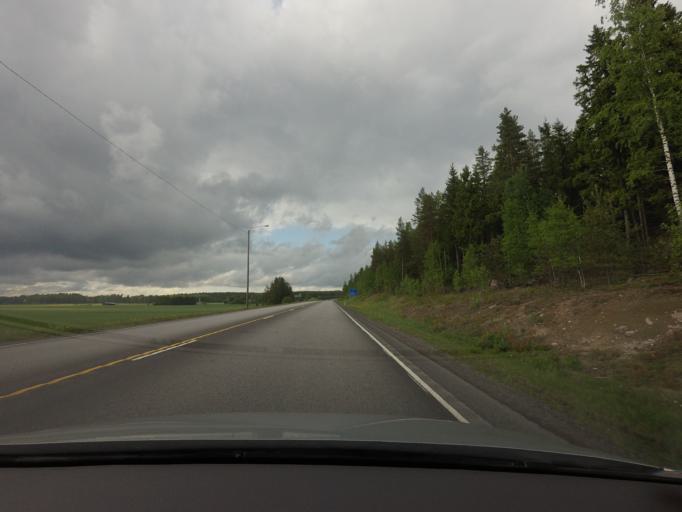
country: FI
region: Uusimaa
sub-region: Loviisa
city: Liljendal
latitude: 60.5745
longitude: 26.0720
